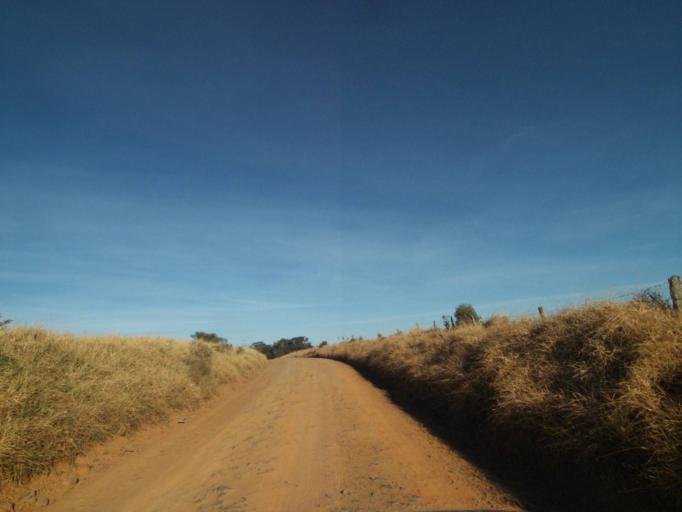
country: BR
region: Parana
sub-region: Telemaco Borba
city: Telemaco Borba
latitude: -24.5310
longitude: -50.6316
